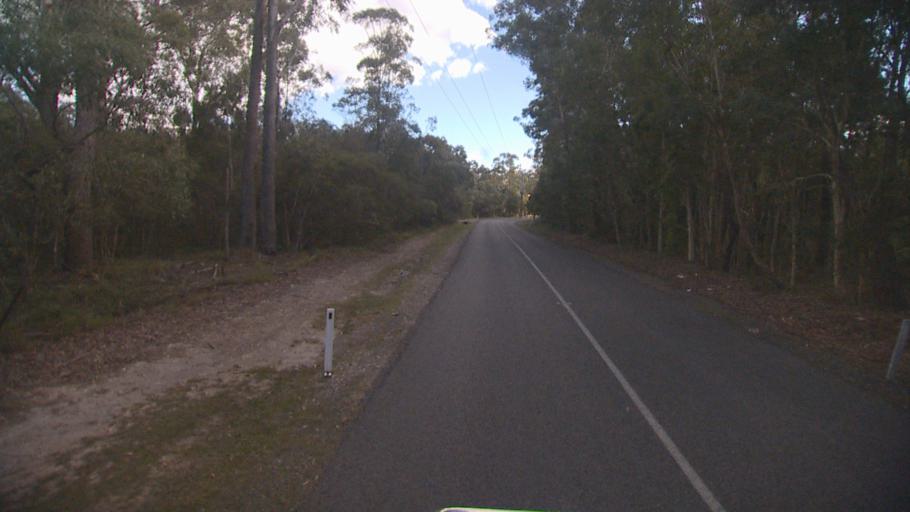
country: AU
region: Queensland
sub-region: Gold Coast
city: Yatala
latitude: -27.6613
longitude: 153.2400
